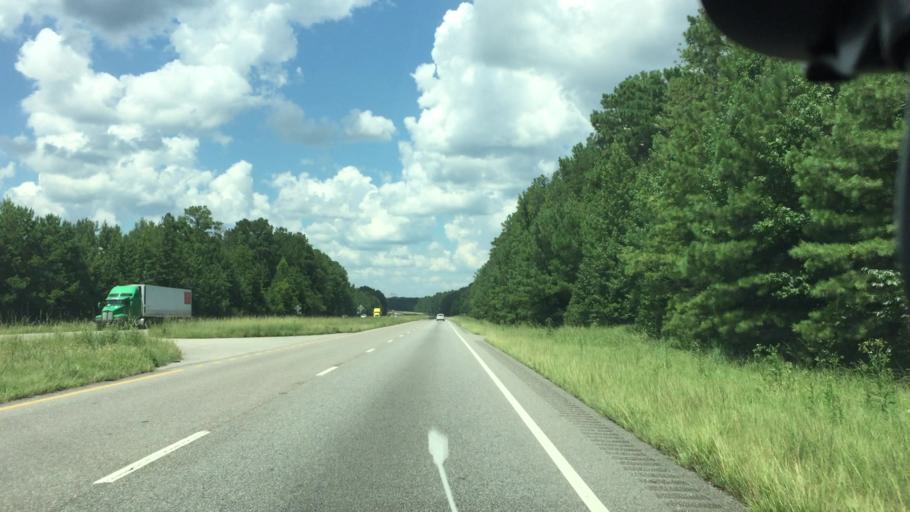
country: US
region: Alabama
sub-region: Pike County
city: Troy
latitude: 31.9851
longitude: -86.0267
